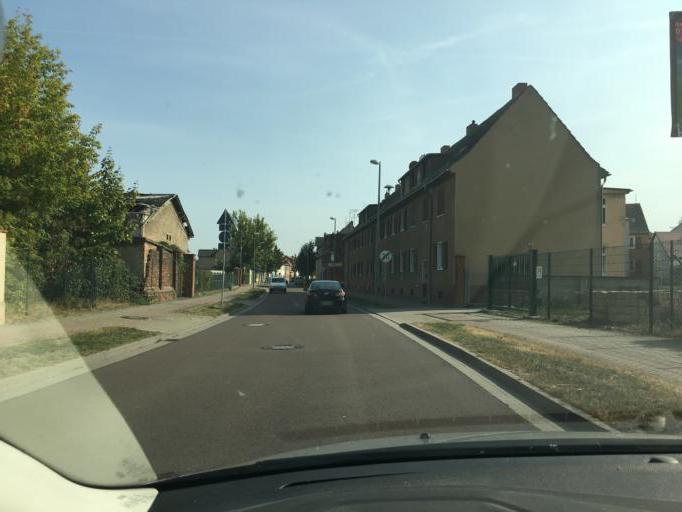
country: DE
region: Saxony-Anhalt
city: Nienburg/Saale
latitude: 51.8431
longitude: 11.7677
